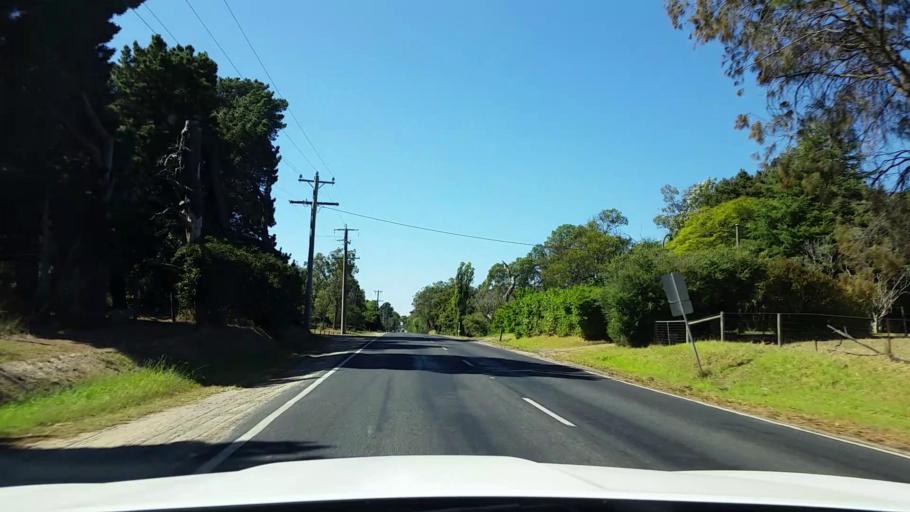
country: AU
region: Victoria
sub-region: Mornington Peninsula
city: Langwarrin South
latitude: -38.1992
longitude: 145.1850
